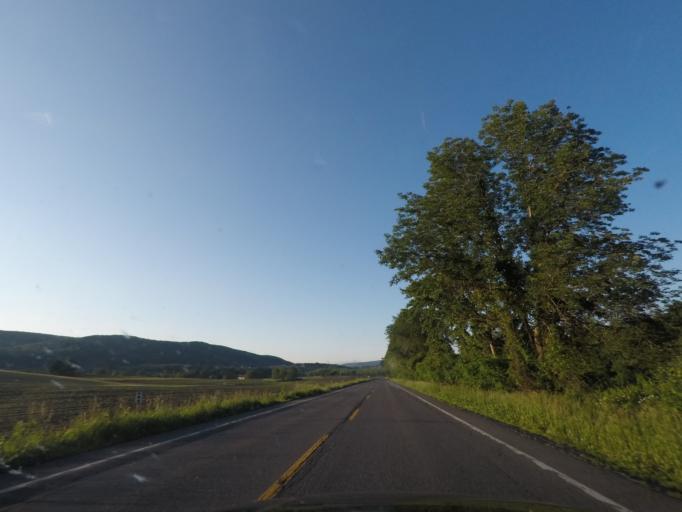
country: US
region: New York
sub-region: Dutchess County
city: Pine Plains
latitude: 41.9999
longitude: -73.5230
